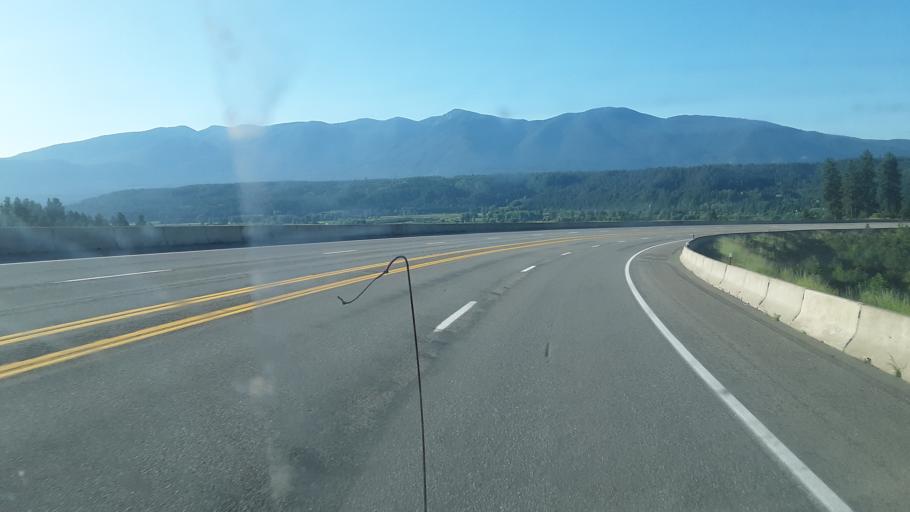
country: US
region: Idaho
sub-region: Boundary County
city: Bonners Ferry
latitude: 48.7130
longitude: -116.3045
